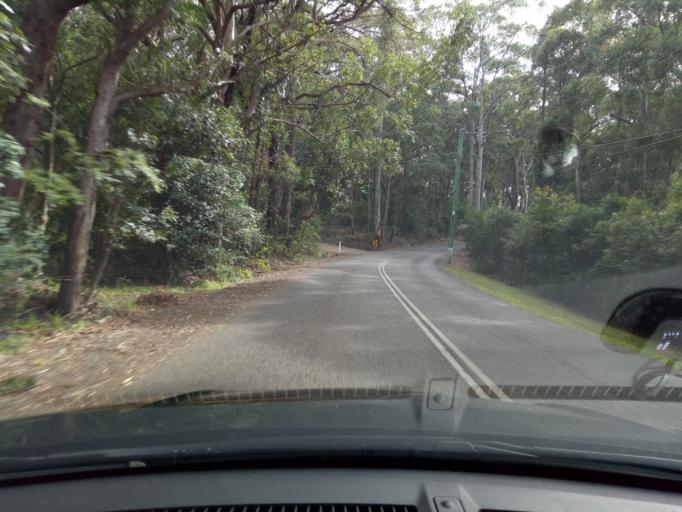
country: AU
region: New South Wales
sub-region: Gosford Shire
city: Holgate
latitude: -33.3856
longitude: 151.4089
